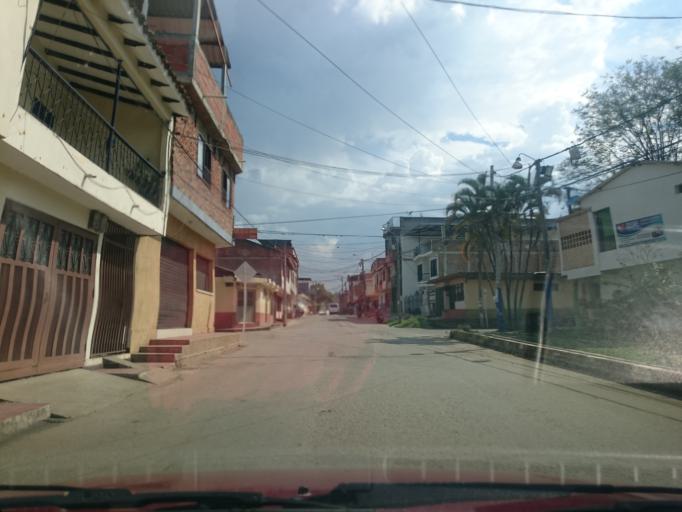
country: CO
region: Cauca
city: Santander de Quilichao
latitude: 3.0126
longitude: -76.4862
